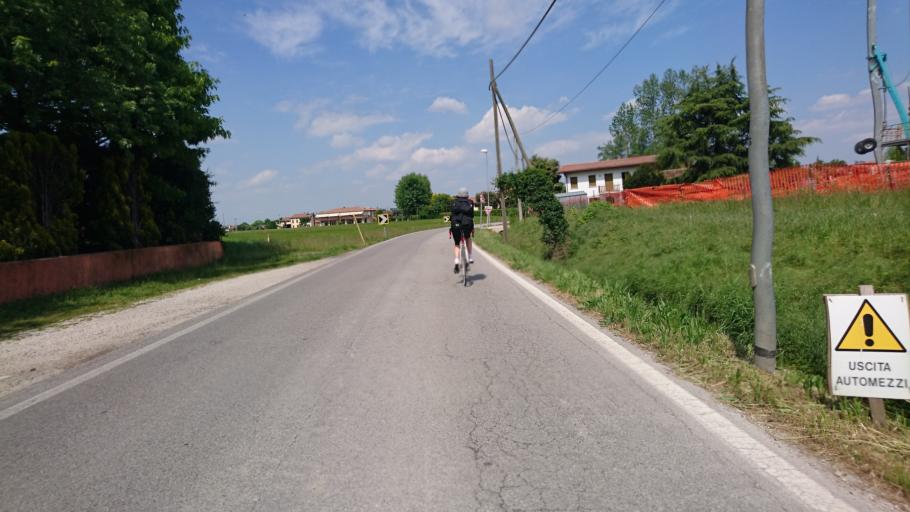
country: IT
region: Veneto
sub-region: Provincia di Padova
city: Saccolongo
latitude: 45.4080
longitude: 11.7334
